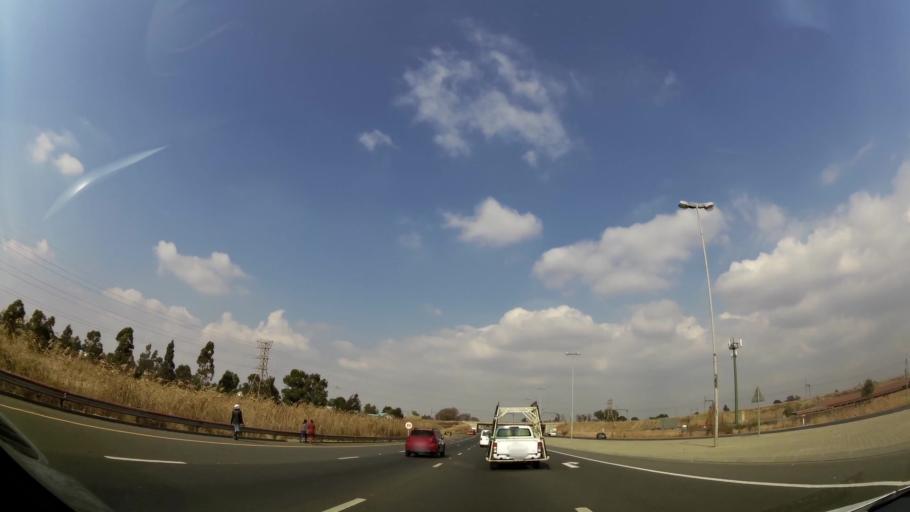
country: ZA
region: Gauteng
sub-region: Ekurhuleni Metropolitan Municipality
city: Brakpan
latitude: -26.1693
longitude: 28.3978
